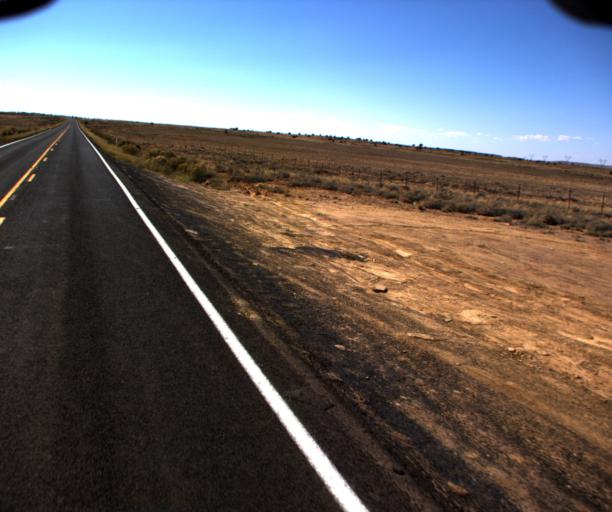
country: US
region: Arizona
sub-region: Coconino County
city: Tuba City
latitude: 35.9677
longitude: -110.8453
